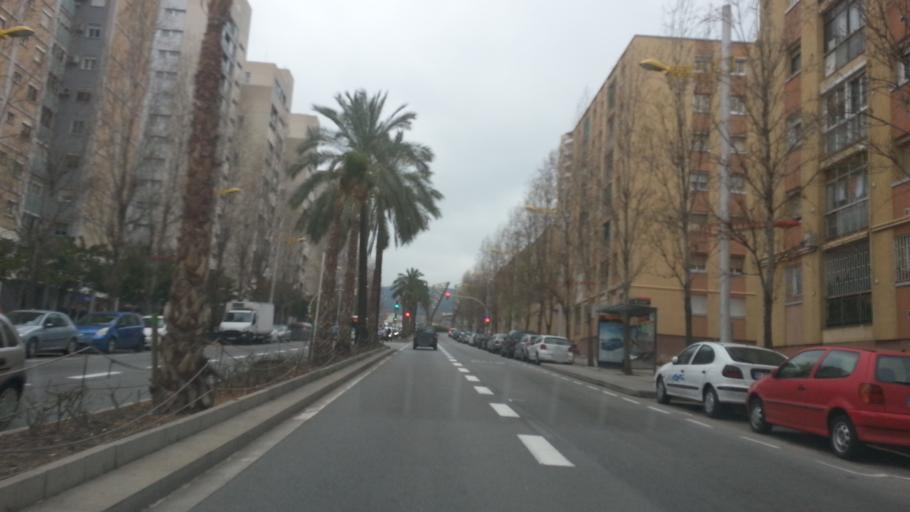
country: ES
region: Catalonia
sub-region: Provincia de Barcelona
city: Nou Barris
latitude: 41.4393
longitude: 2.1659
